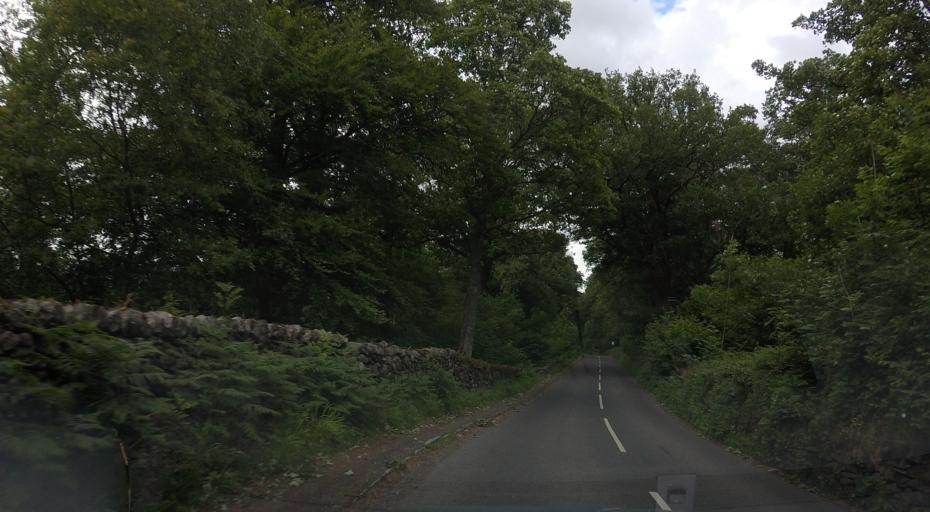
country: GB
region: England
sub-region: Cumbria
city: Keswick
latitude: 54.5814
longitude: -3.1309
